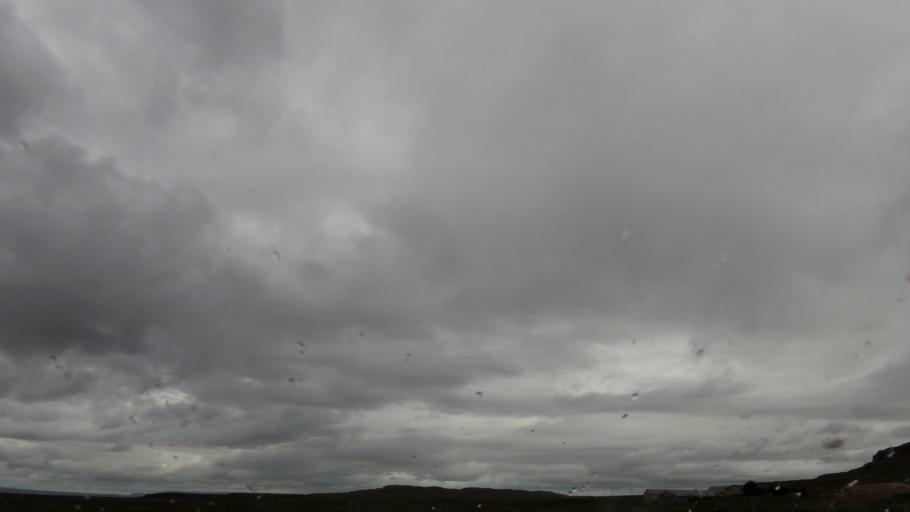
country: IS
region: West
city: Borgarnes
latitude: 65.0232
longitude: -22.1007
